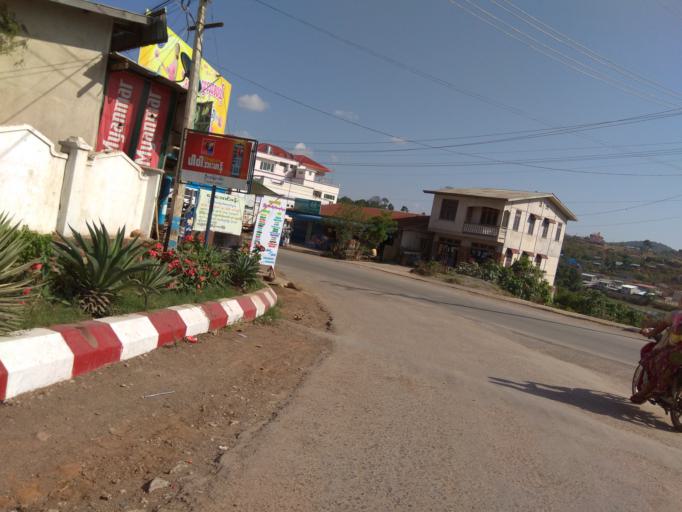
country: MM
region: Shan
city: Taunggyi
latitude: 20.6563
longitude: 96.6376
